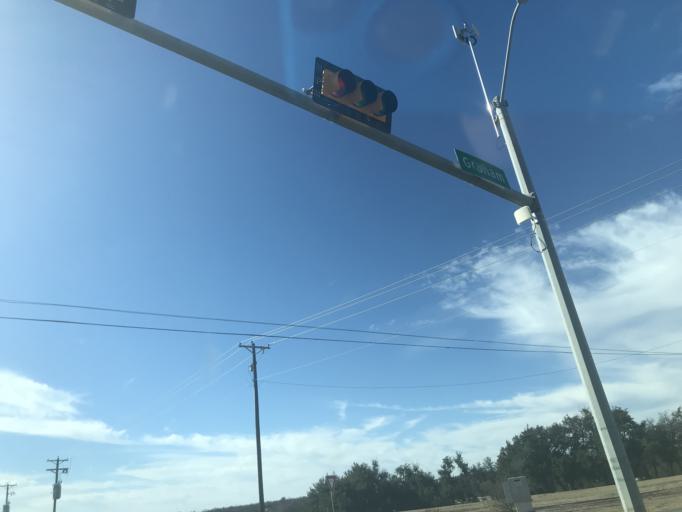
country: US
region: Texas
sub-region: Erath County
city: Stephenville
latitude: 32.2119
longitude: -98.1962
